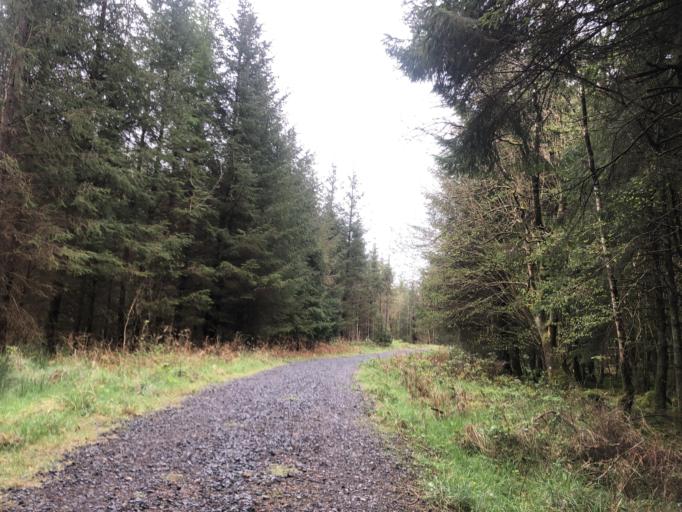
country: IE
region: Connaught
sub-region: Roscommon
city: Boyle
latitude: 53.9850
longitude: -8.1961
